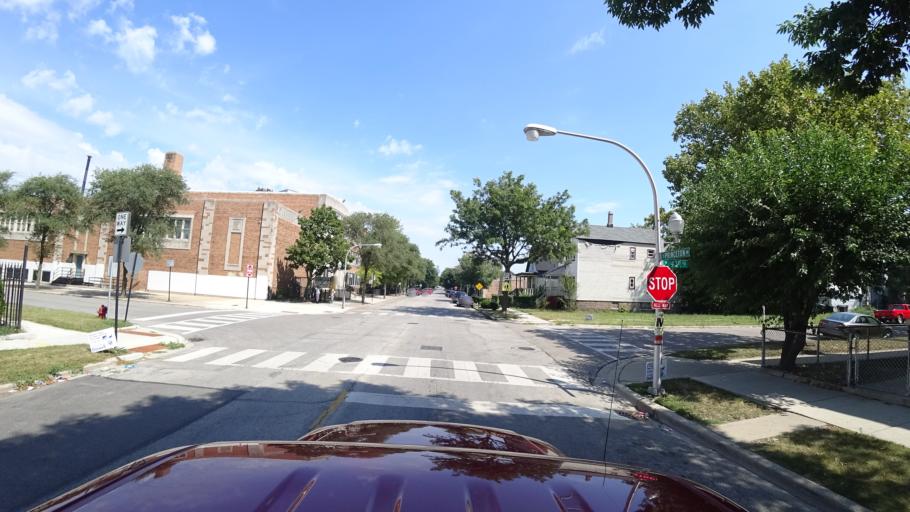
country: US
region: Illinois
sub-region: Cook County
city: Chicago
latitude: 41.8153
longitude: -87.6336
